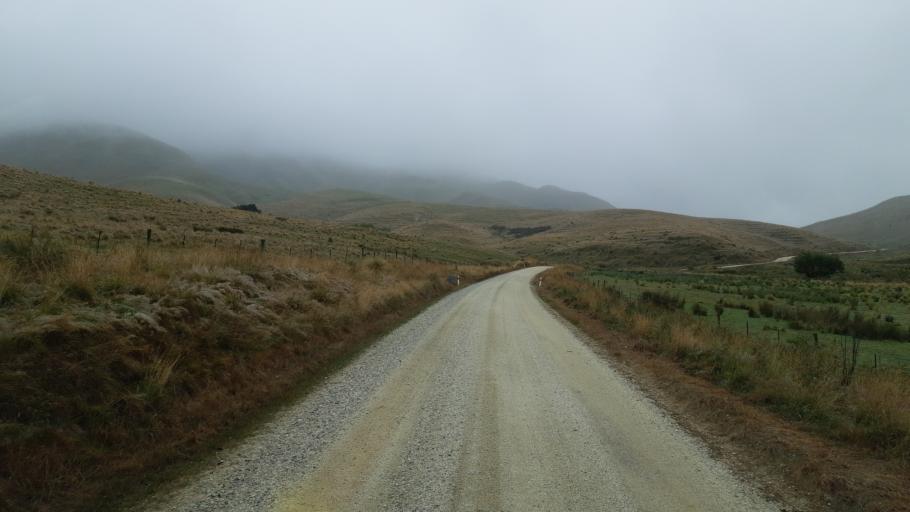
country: NZ
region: Otago
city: Oamaru
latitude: -44.9728
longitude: 170.4914
